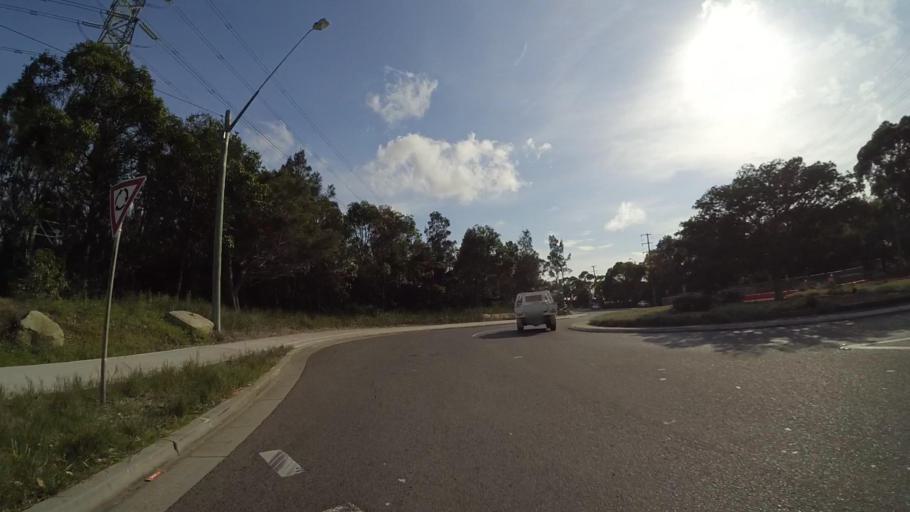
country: AU
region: New South Wales
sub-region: Sutherland Shire
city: Cronulla
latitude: -34.0392
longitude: 151.1563
